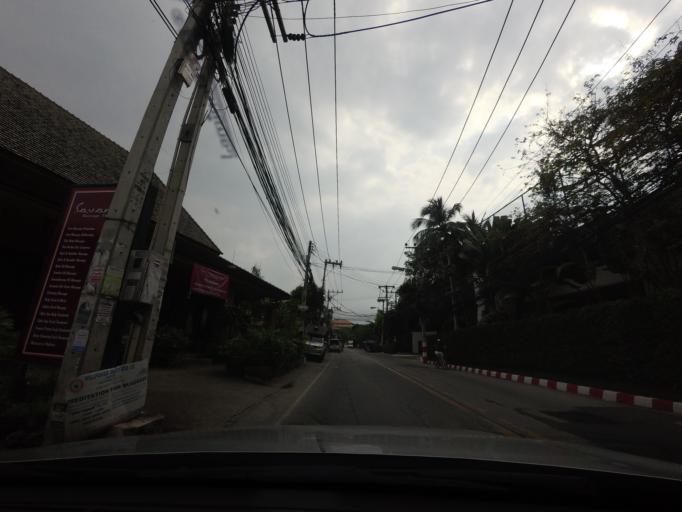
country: TH
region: Chon Buri
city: Phatthaya
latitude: 12.9608
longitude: 100.8868
